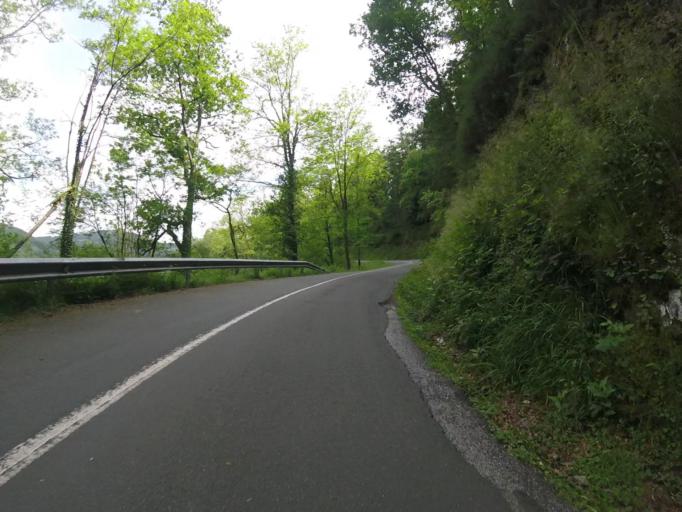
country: ES
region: Navarre
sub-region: Provincia de Navarra
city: Arano
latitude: 43.2569
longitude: -1.8498
